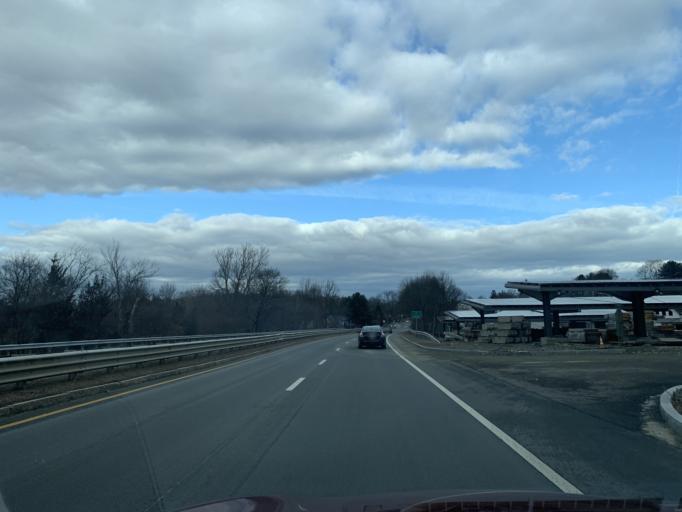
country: US
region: Massachusetts
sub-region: Essex County
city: Newburyport
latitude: 42.8045
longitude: -70.8789
